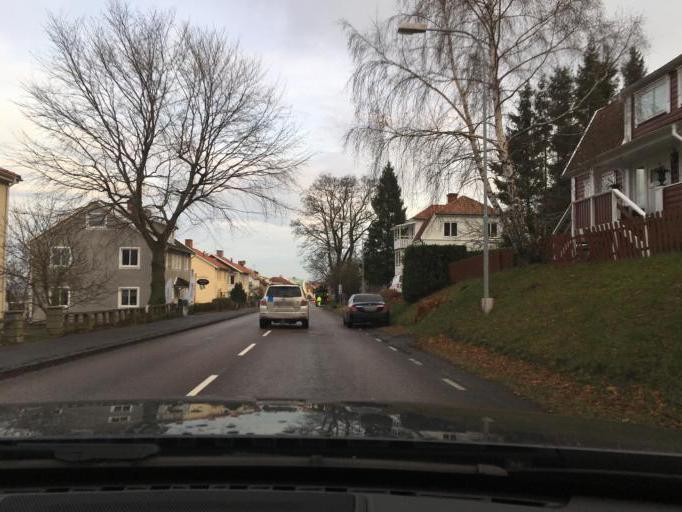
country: SE
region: Joenkoeping
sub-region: Jonkopings Kommun
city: Graenna
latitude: 58.0165
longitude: 14.4609
